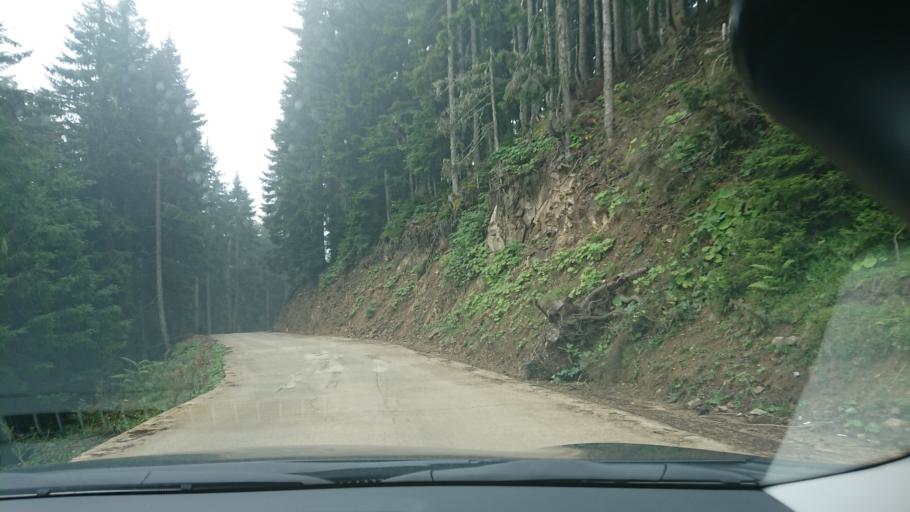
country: TR
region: Gumushane
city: Kurtun
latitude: 40.6664
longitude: 39.0117
